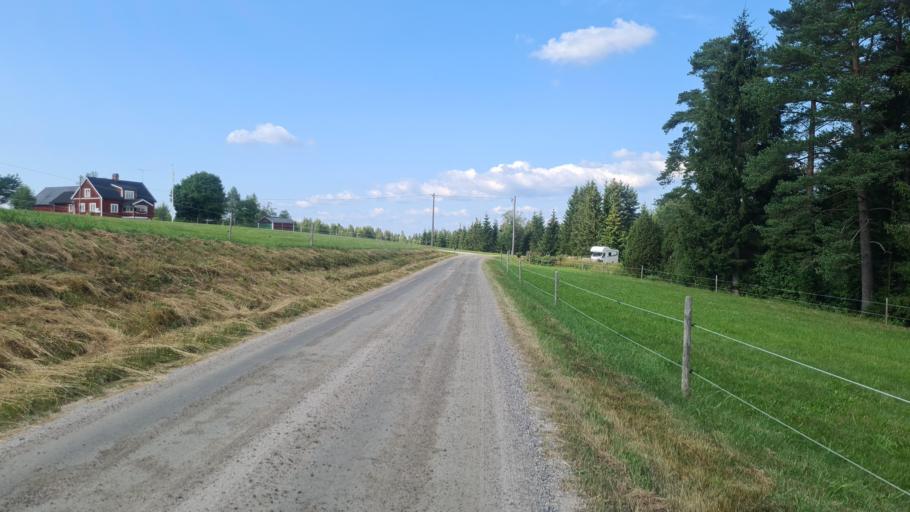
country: SE
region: Kronoberg
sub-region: Ljungby Kommun
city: Ljungby
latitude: 56.7200
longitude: 13.8812
